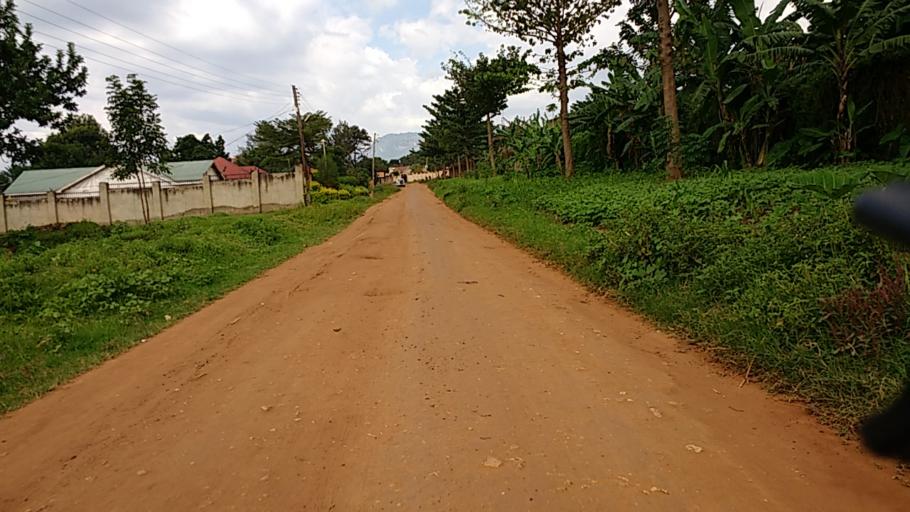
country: UG
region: Eastern Region
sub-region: Mbale District
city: Mbale
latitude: 1.0713
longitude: 34.1677
